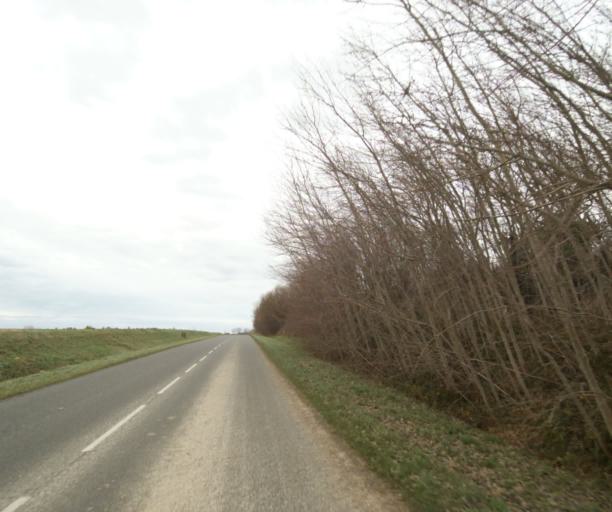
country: FR
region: Nord-Pas-de-Calais
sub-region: Departement du Nord
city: Jenlain
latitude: 50.3266
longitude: 3.6332
